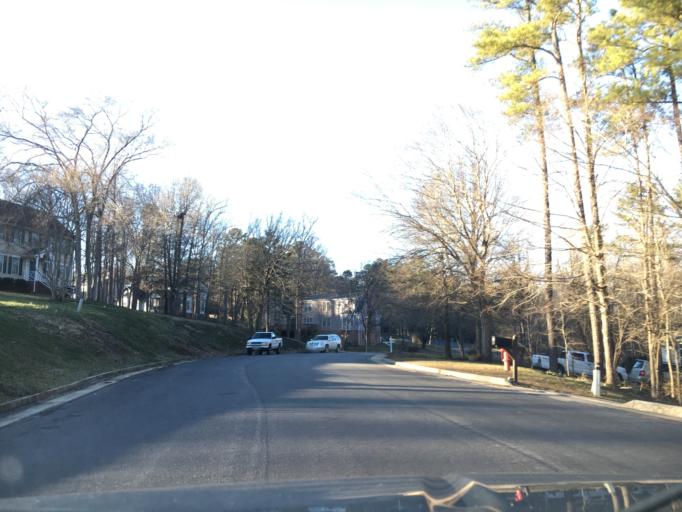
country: US
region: Virginia
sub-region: Halifax County
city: South Boston
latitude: 36.7051
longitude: -78.8816
